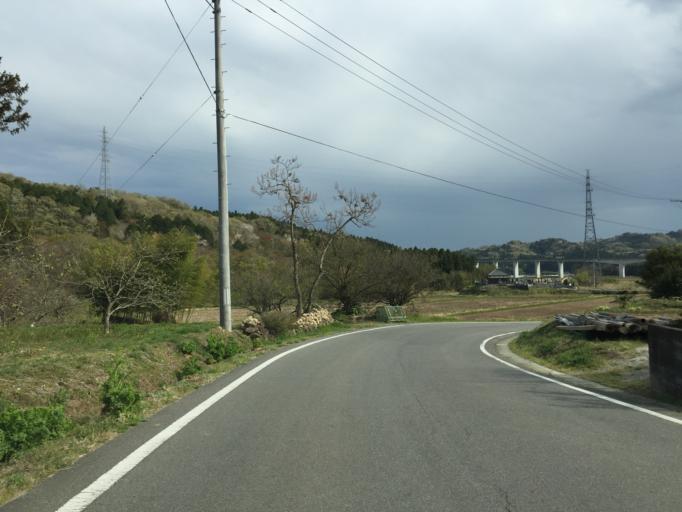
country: JP
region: Fukushima
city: Iwaki
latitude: 37.1252
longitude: 140.9029
